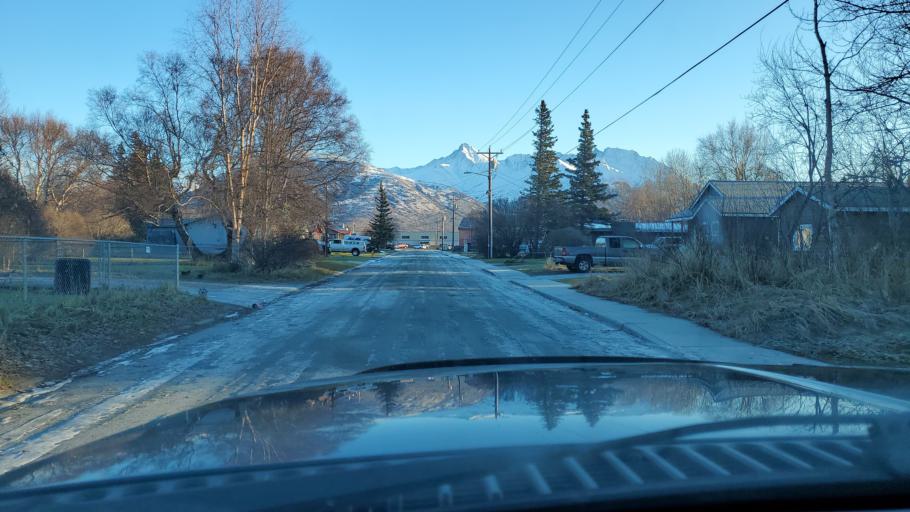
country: US
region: Alaska
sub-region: Matanuska-Susitna Borough
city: Palmer
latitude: 61.6109
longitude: -149.1072
